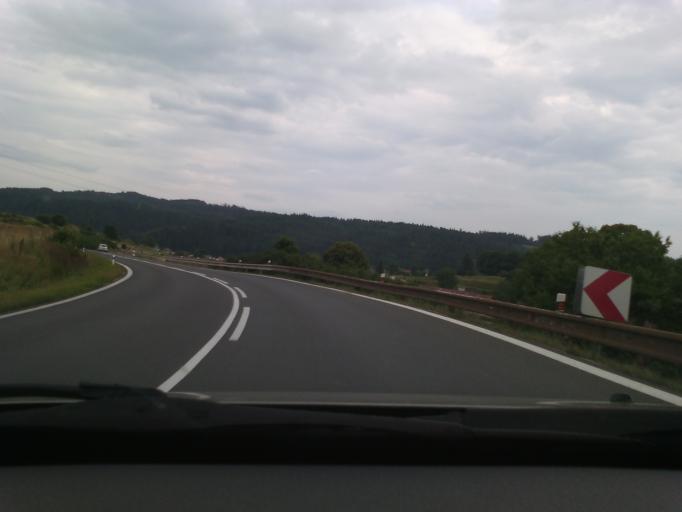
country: SK
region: Presovsky
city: Spisska Bela
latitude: 49.1784
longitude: 20.4512
